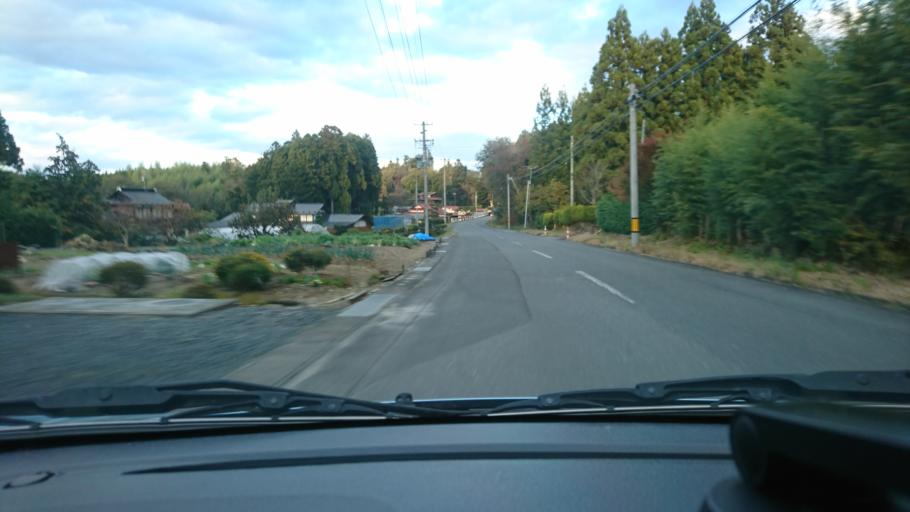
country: JP
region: Iwate
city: Ichinoseki
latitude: 38.7909
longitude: 141.1875
